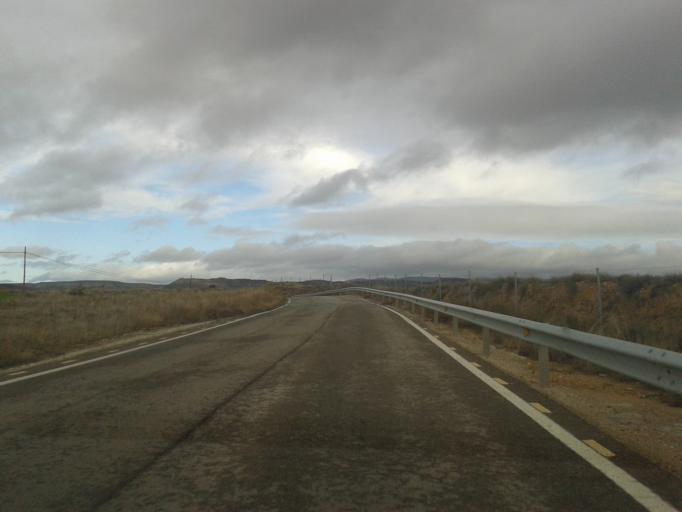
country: ES
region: Aragon
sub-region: Provincia de Teruel
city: Calamocha
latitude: 40.9190
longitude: -1.2704
